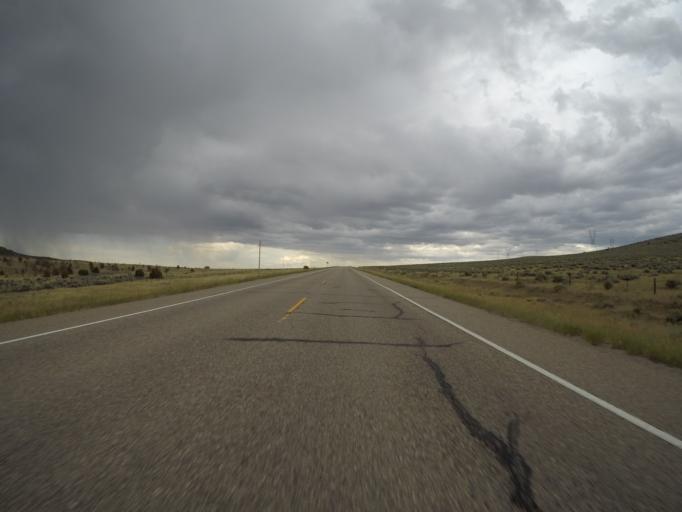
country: US
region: Colorado
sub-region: Rio Blanco County
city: Rangely
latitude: 40.3712
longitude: -108.3861
